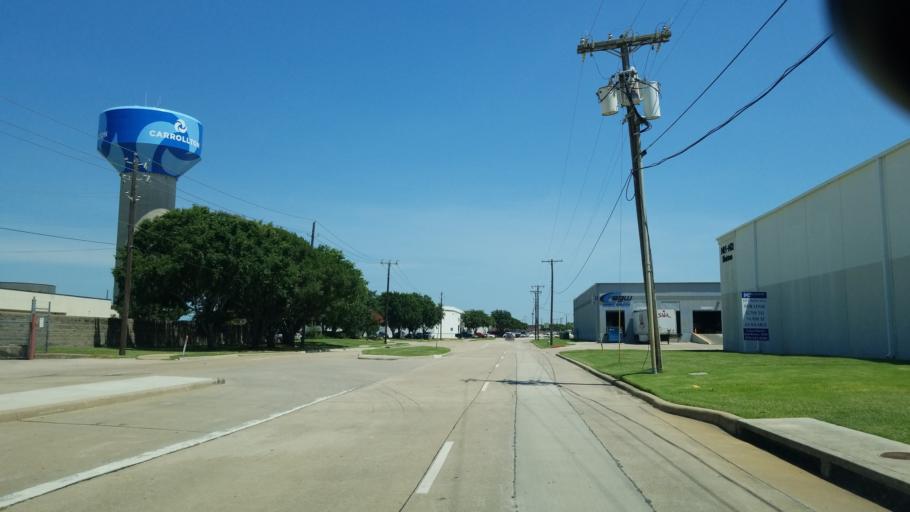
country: US
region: Texas
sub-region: Dallas County
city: Carrollton
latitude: 32.9473
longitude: -96.9166
